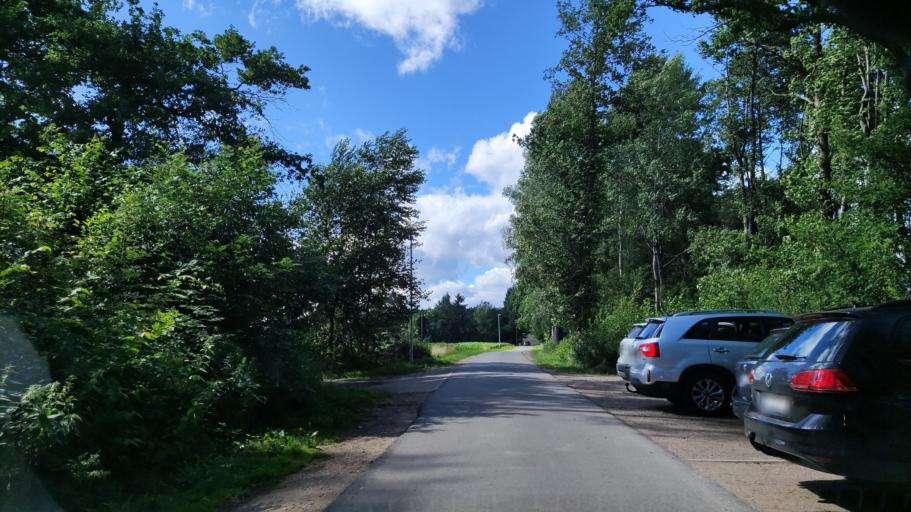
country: DE
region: Lower Saxony
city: Amelinghausen
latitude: 53.1310
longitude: 10.2301
